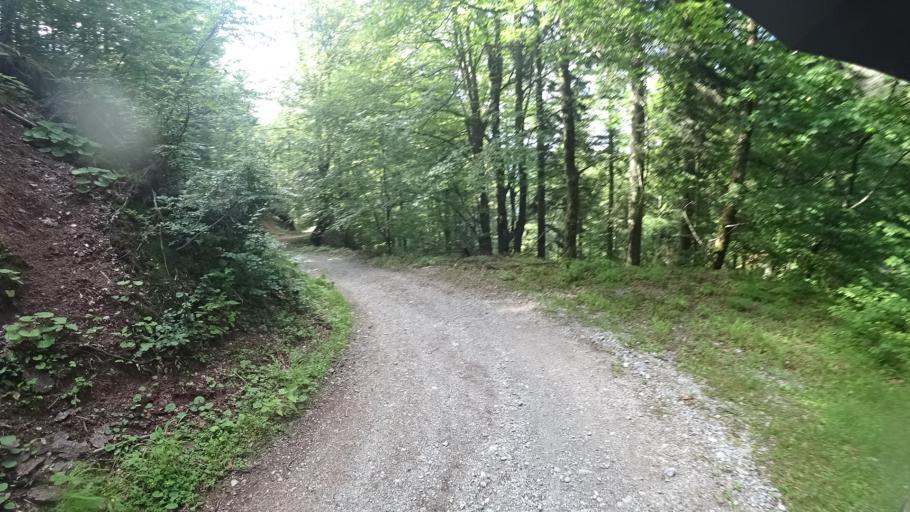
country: SI
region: Osilnica
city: Osilnica
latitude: 45.4698
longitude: 14.7000
